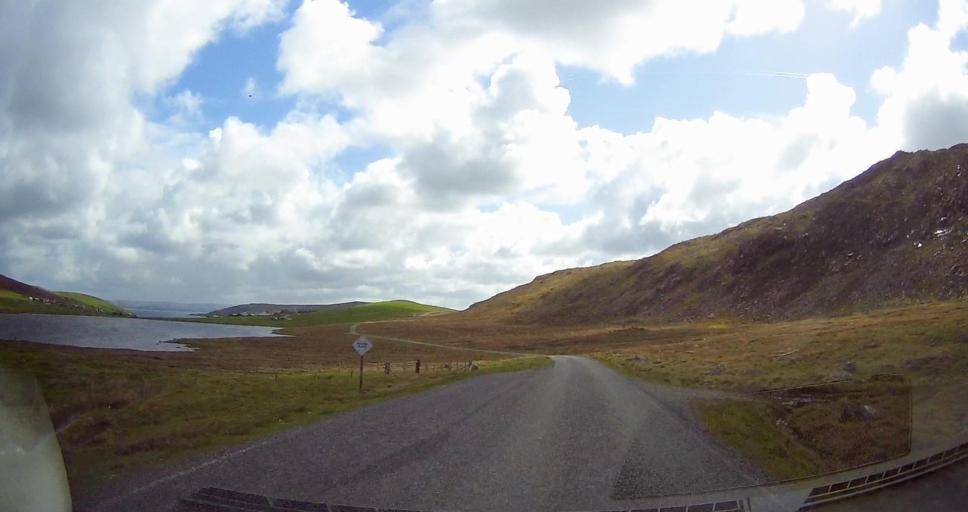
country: GB
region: Scotland
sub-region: Shetland Islands
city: Lerwick
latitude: 60.5519
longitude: -1.3398
